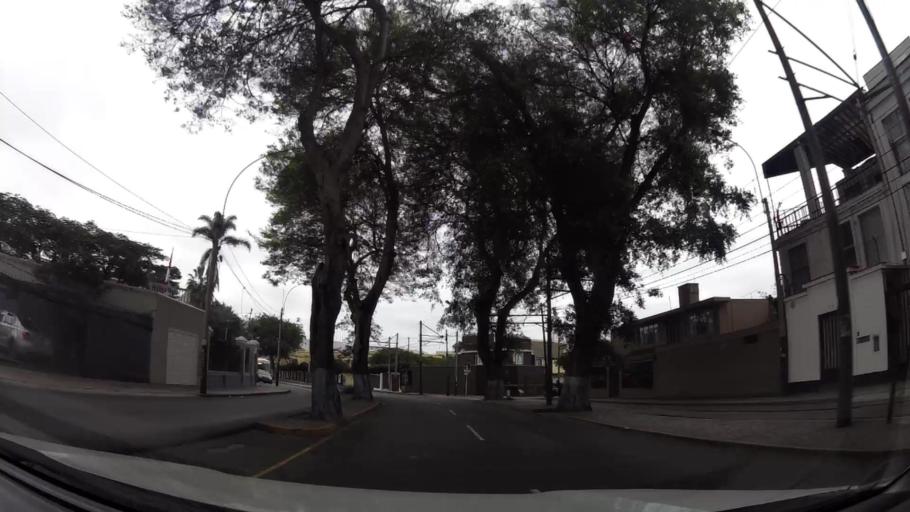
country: PE
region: Lima
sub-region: Lima
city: Surco
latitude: -12.1539
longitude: -77.0231
